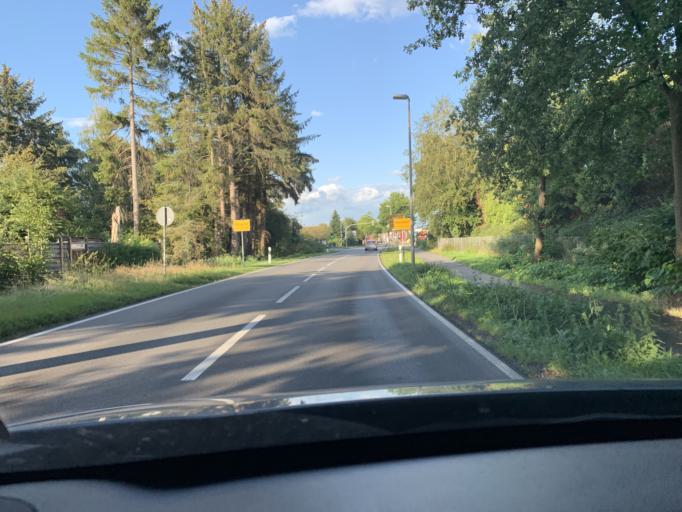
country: DE
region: Lower Saxony
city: Edewecht
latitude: 53.1162
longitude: 7.9666
